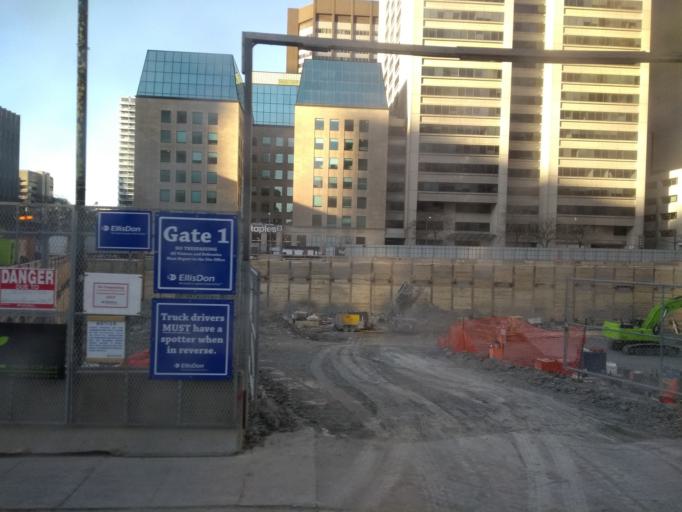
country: CA
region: Ontario
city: Toronto
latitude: 43.6541
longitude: -79.3857
